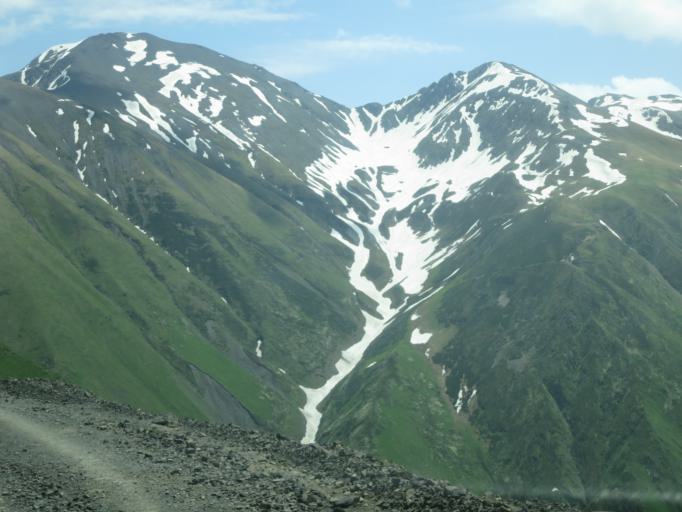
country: GE
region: Kakheti
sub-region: Telavi
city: Telavi
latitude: 42.2720
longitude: 45.4942
